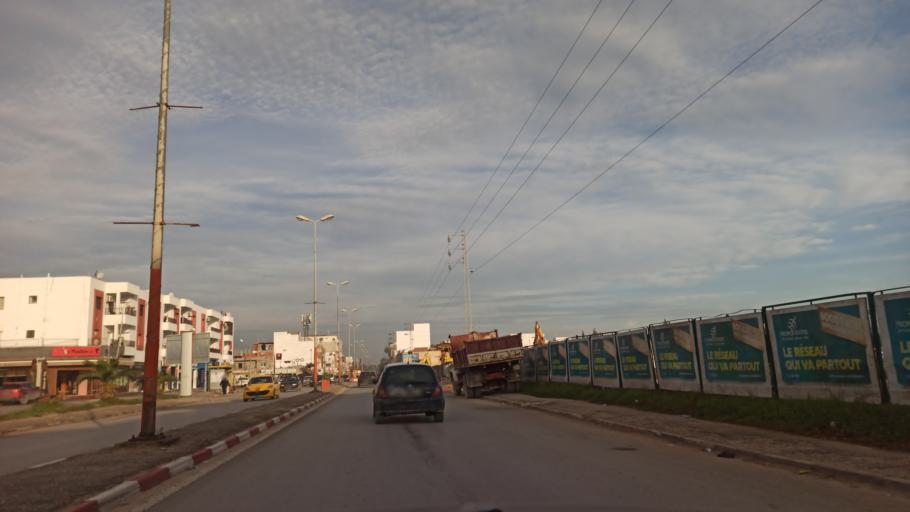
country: TN
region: Ariana
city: Ariana
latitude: 36.8642
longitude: 10.2529
